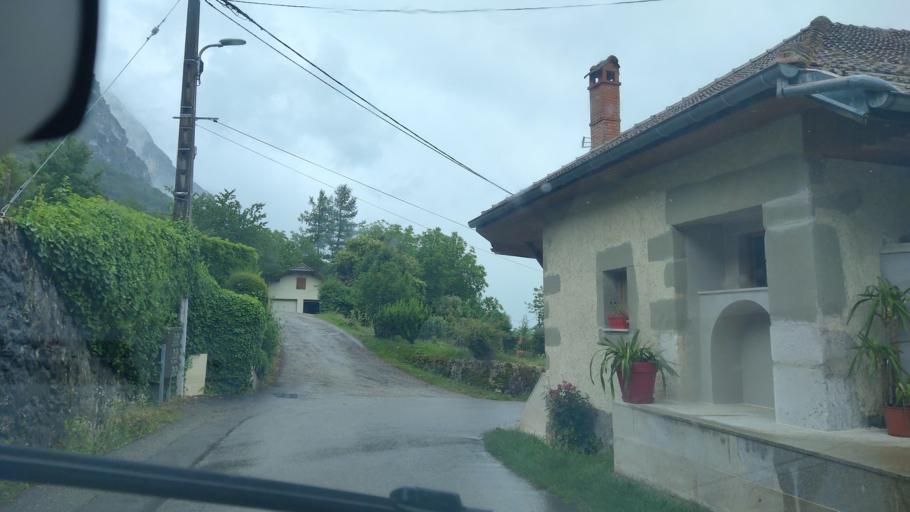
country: FR
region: Rhone-Alpes
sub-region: Departement de la Savoie
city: Chindrieux
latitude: 45.8191
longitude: 5.8531
